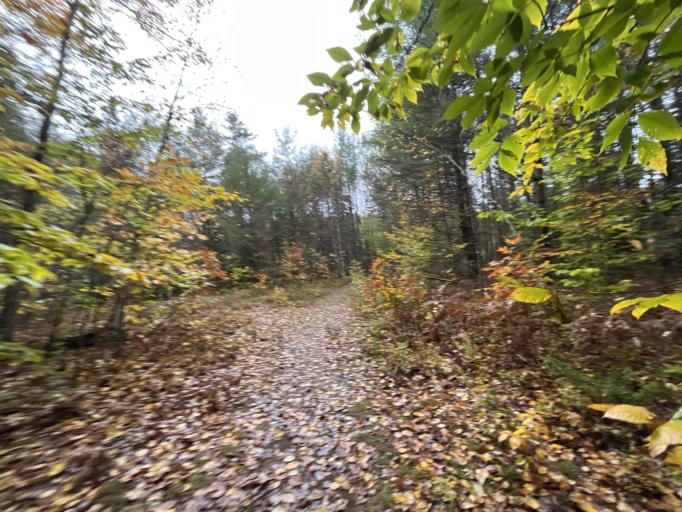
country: US
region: New Hampshire
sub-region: Merrimack County
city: New London
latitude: 43.3982
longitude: -71.9991
